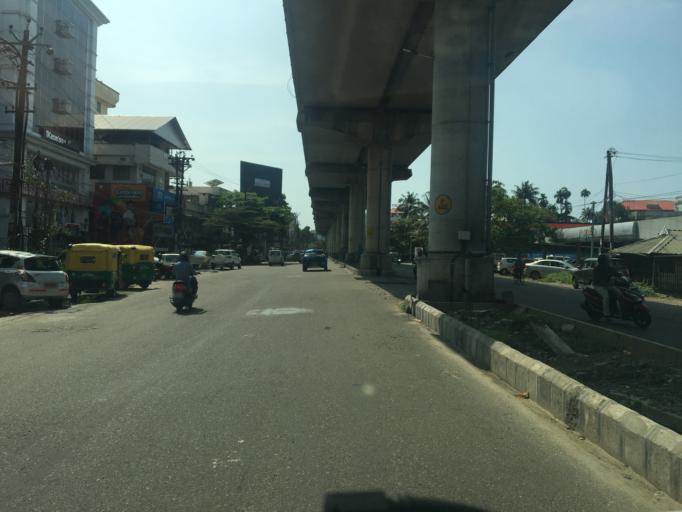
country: IN
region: Kerala
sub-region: Ernakulam
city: Cochin
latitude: 9.9682
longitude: 76.3138
